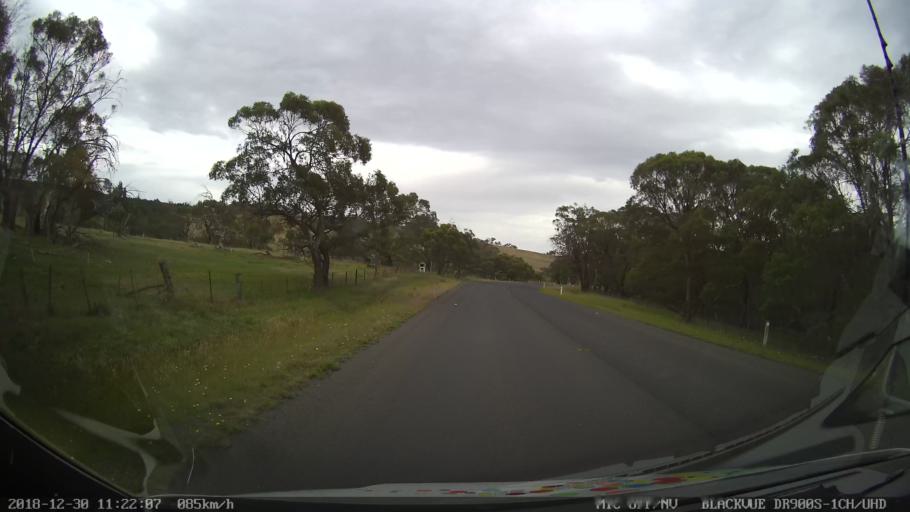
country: AU
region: New South Wales
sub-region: Snowy River
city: Jindabyne
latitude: -36.5038
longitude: 148.6710
